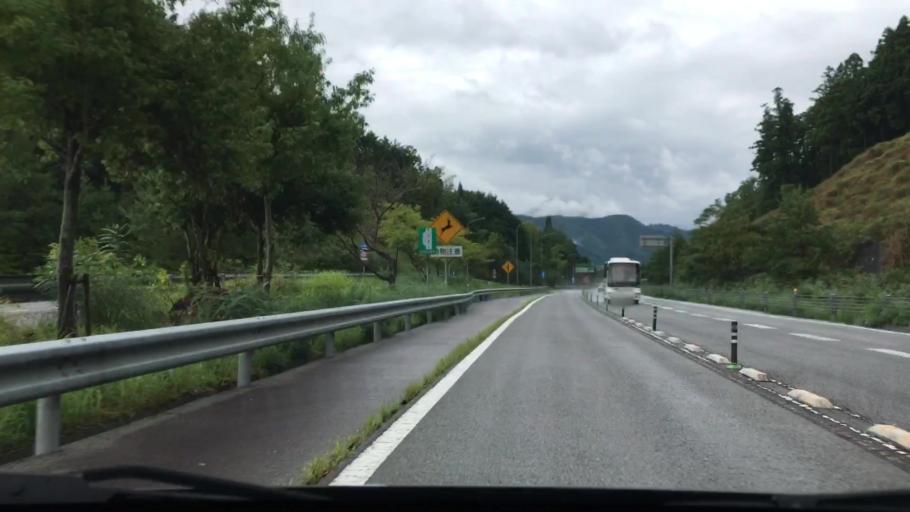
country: JP
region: Hyogo
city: Toyooka
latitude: 35.2944
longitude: 134.8252
